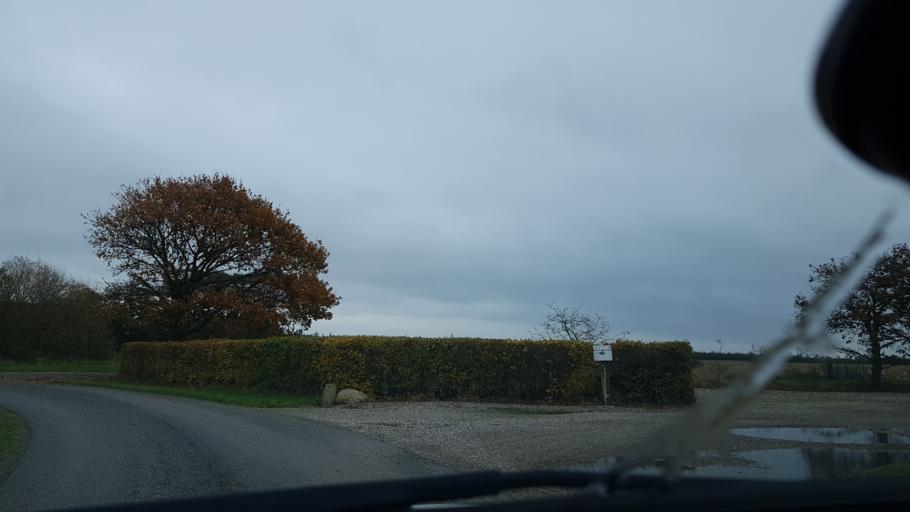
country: DK
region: South Denmark
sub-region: Esbjerg Kommune
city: Ribe
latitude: 55.2559
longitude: 8.8365
